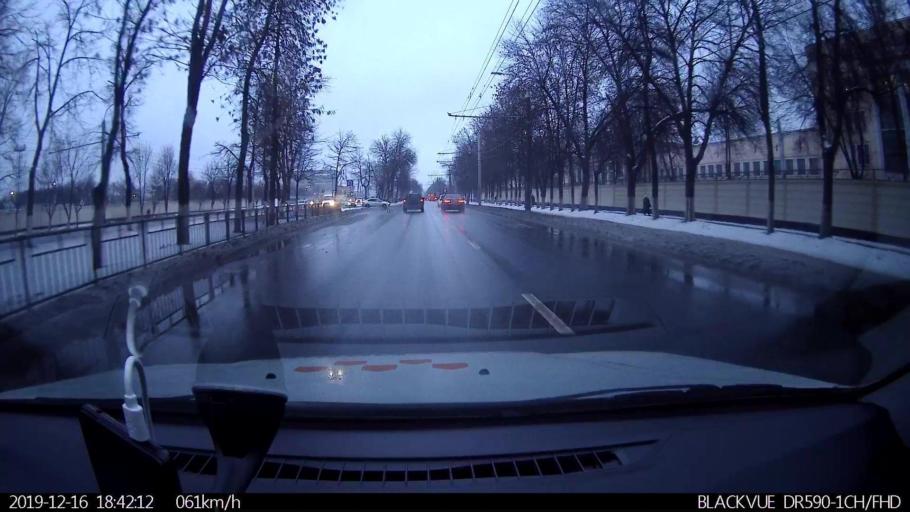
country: RU
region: Nizjnij Novgorod
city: Nizhniy Novgorod
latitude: 56.2509
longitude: 43.8870
